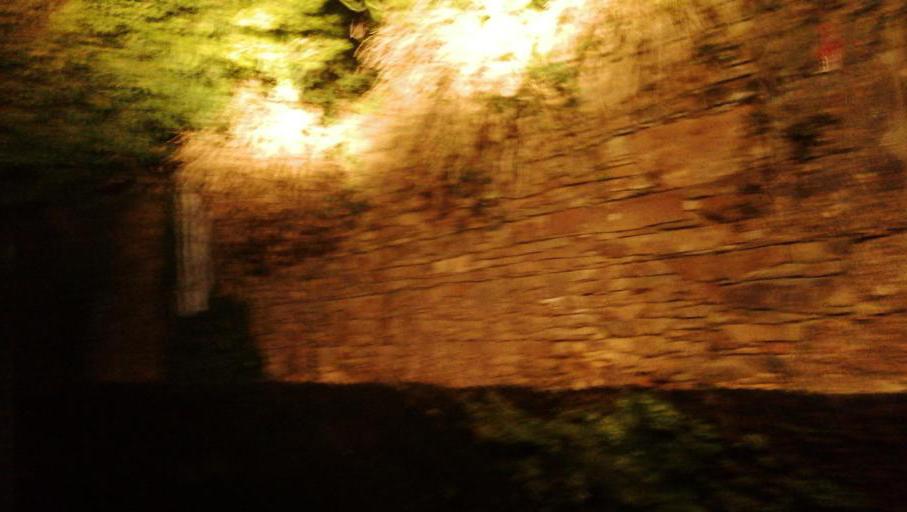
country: FR
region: Brittany
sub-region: Departement des Cotes-d'Armor
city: Lanvollon
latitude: 48.6379
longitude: -3.0016
